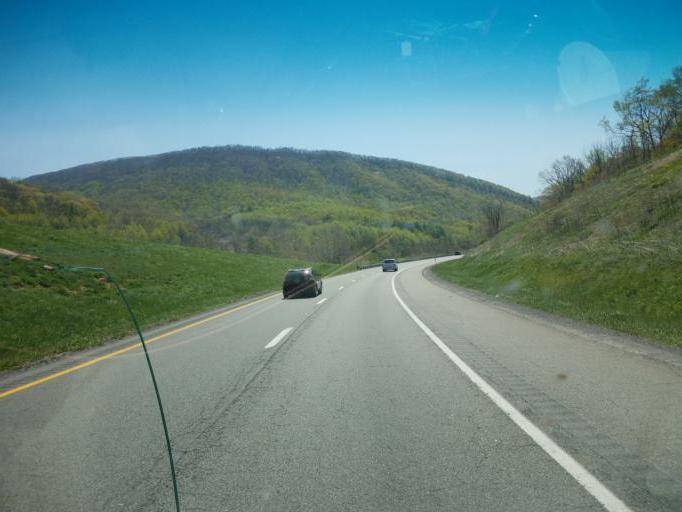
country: US
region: West Virginia
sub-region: Mercer County
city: Bluefield
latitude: 37.2368
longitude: -81.0989
